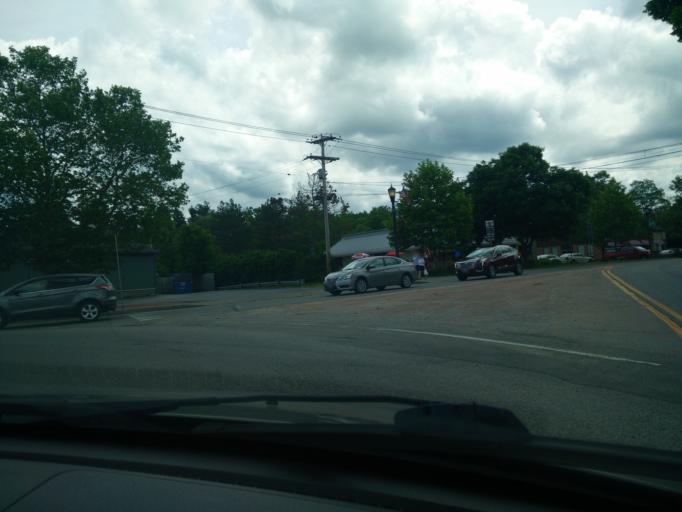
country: US
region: New York
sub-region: Erie County
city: East Aurora
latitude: 42.7678
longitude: -78.6294
